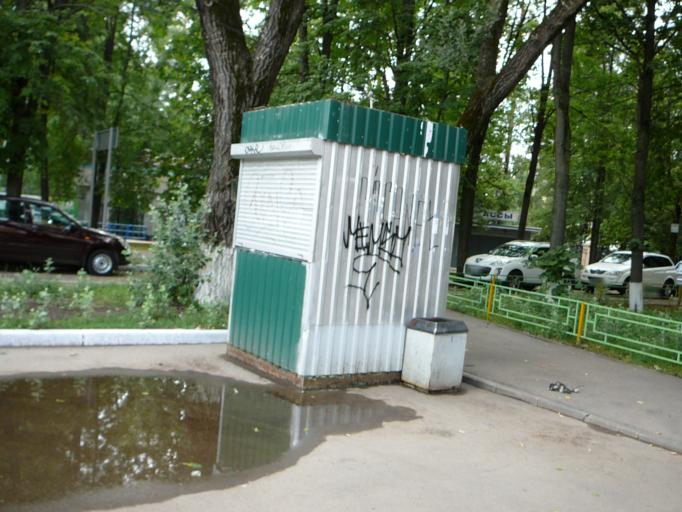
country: RU
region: Moskovskaya
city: Krasnogorsk
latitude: 55.8279
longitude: 37.3297
